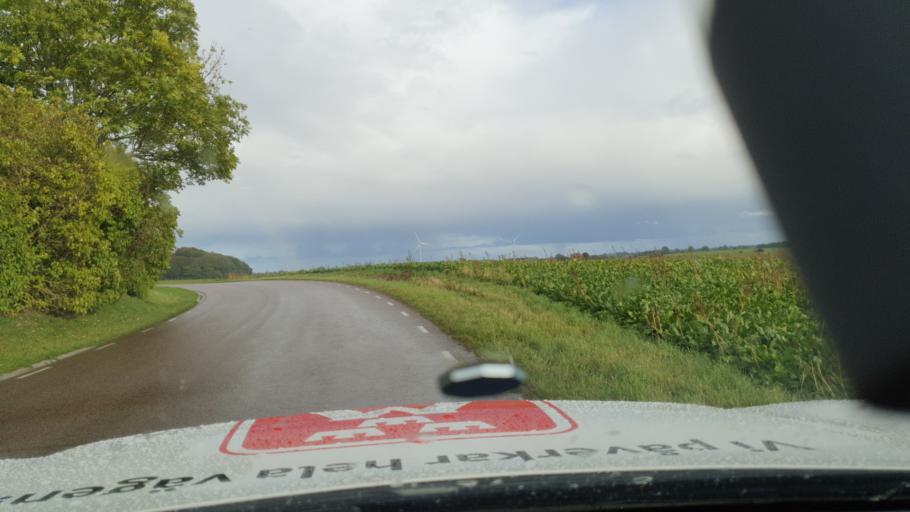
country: SE
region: Skane
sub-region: Malmo
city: Oxie
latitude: 55.5244
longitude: 13.1162
